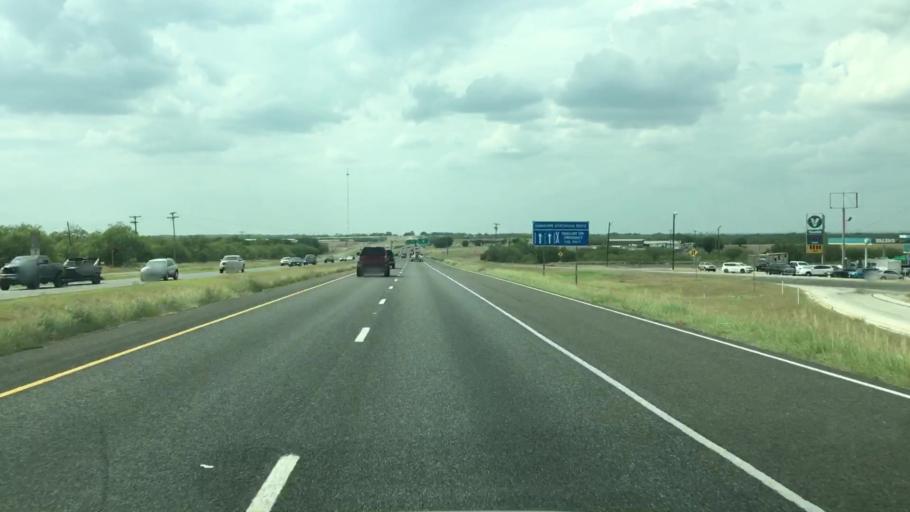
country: US
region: Texas
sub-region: Atascosa County
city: Pleasanton
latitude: 28.9032
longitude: -98.4251
